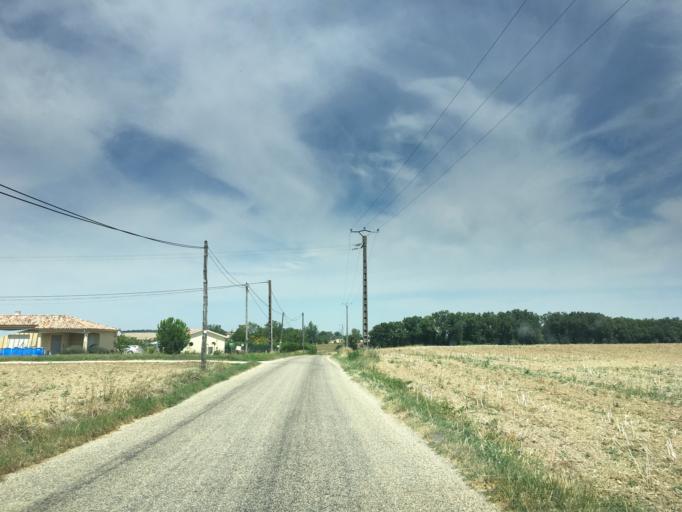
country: FR
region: Midi-Pyrenees
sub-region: Departement du Gers
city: Jegun
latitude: 43.8055
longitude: 0.4999
